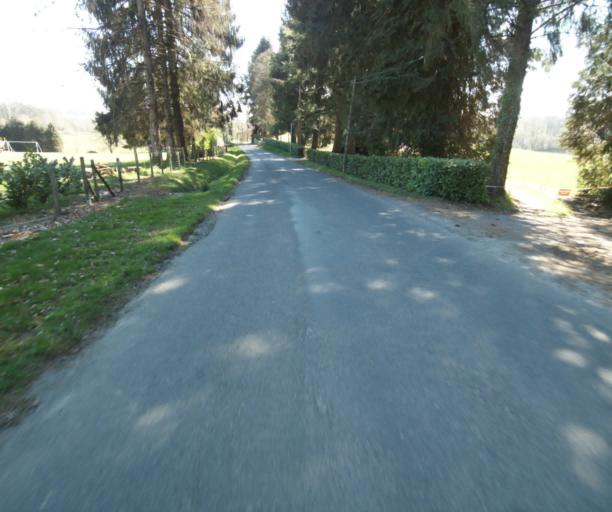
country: FR
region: Limousin
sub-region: Departement de la Correze
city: Saint-Clement
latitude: 45.3013
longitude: 1.7007
